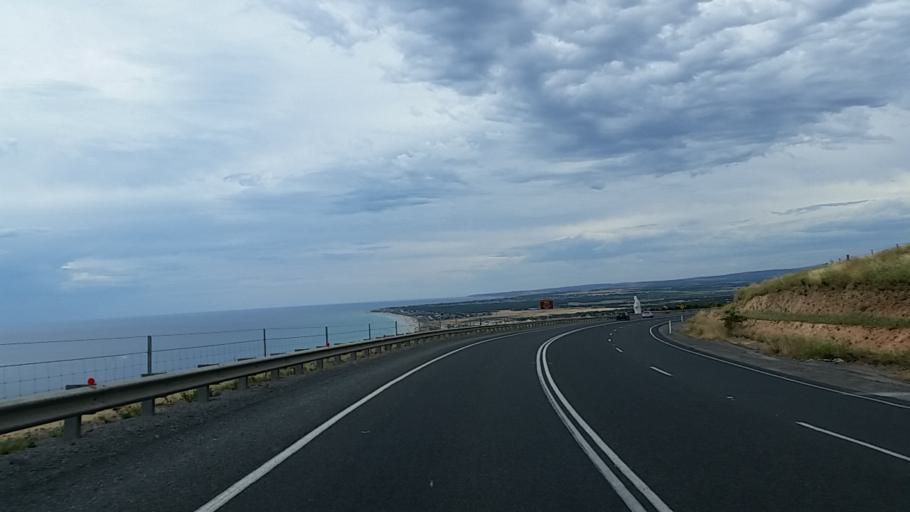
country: AU
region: South Australia
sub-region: Onkaparinga
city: Port Willunga
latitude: -35.3541
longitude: 138.4475
